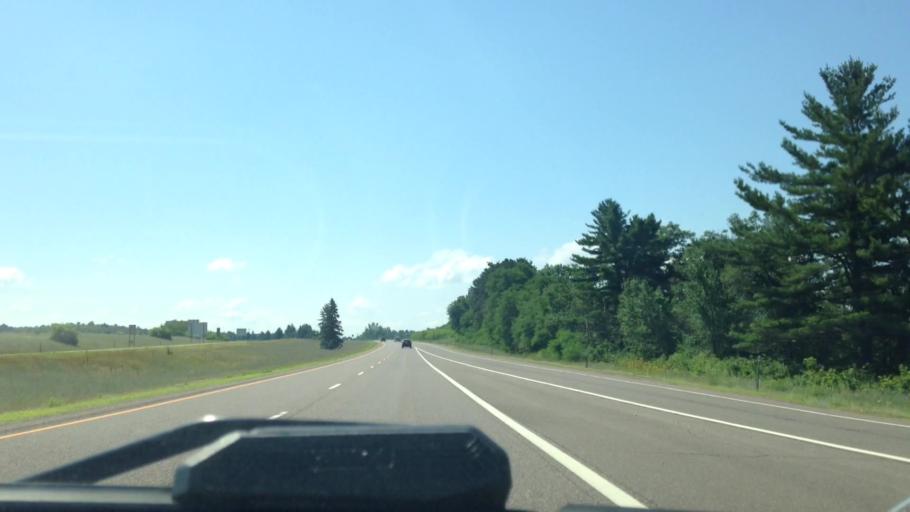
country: US
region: Wisconsin
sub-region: Barron County
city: Cameron
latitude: 45.3916
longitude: -91.7573
